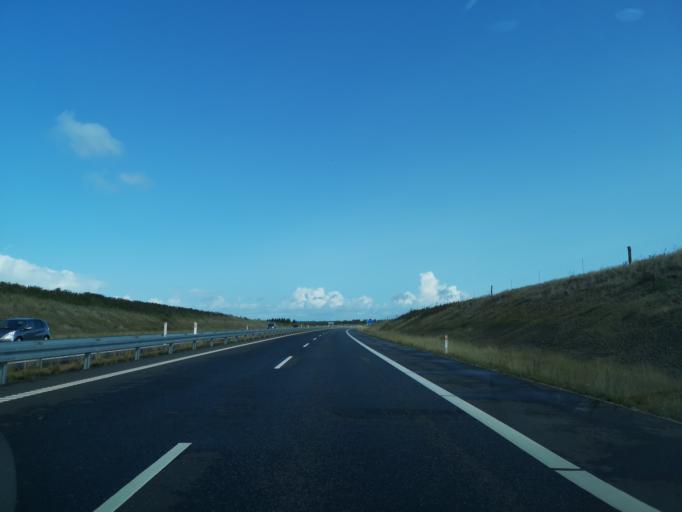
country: DK
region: Central Jutland
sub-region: Herning Kommune
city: Snejbjerg
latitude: 56.1367
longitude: 8.8696
